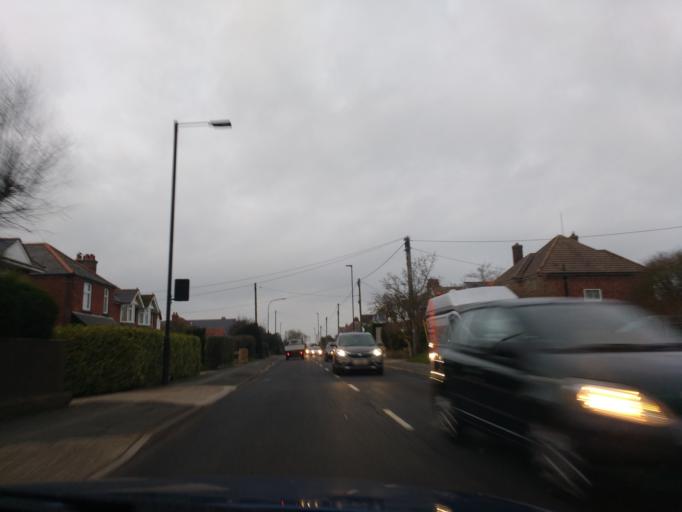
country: GB
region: England
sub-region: Isle of Wight
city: Northwood
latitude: 50.7528
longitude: -1.3134
